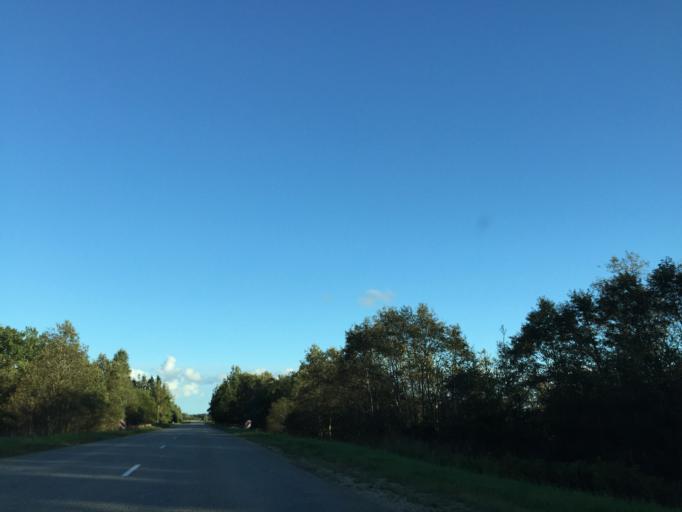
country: LV
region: Kuldigas Rajons
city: Kuldiga
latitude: 56.9434
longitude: 22.0212
